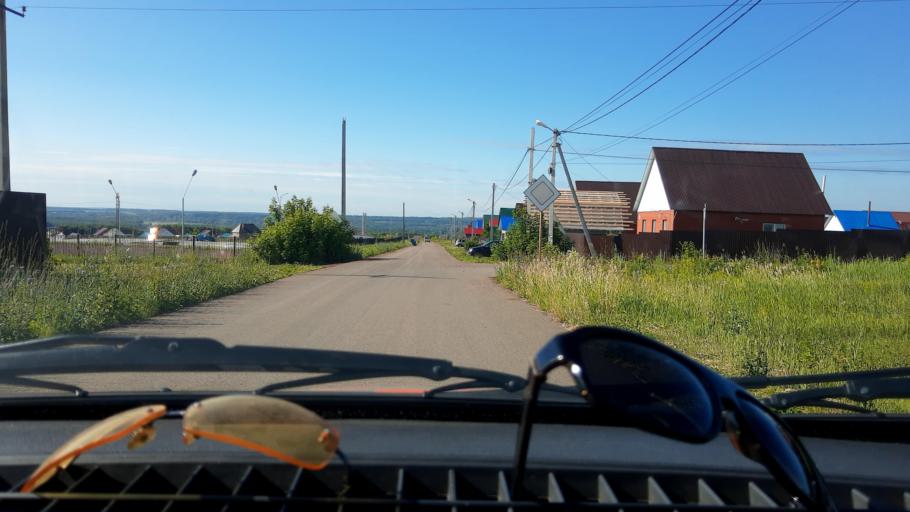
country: RU
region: Bashkortostan
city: Avdon
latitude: 54.6534
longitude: 55.7376
